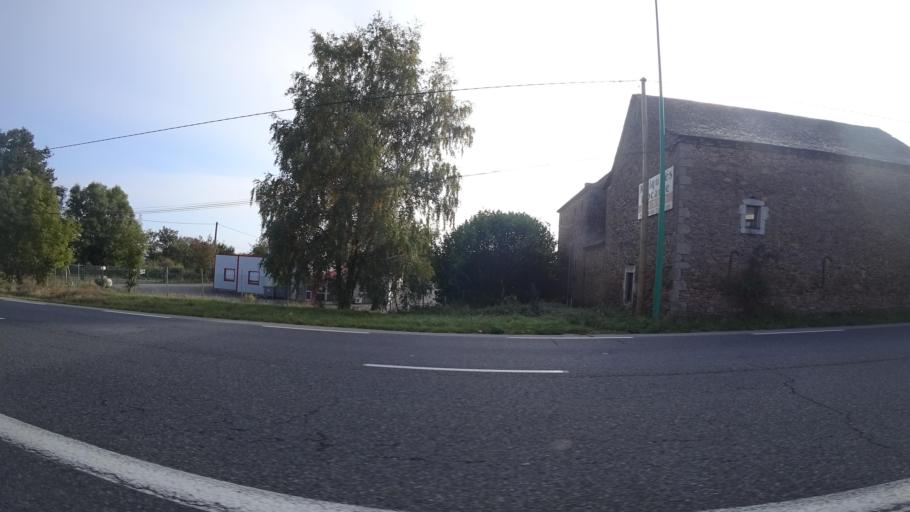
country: FR
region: Midi-Pyrenees
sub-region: Departement de l'Aveyron
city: Luc-la-Primaube
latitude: 44.3050
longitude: 2.5571
